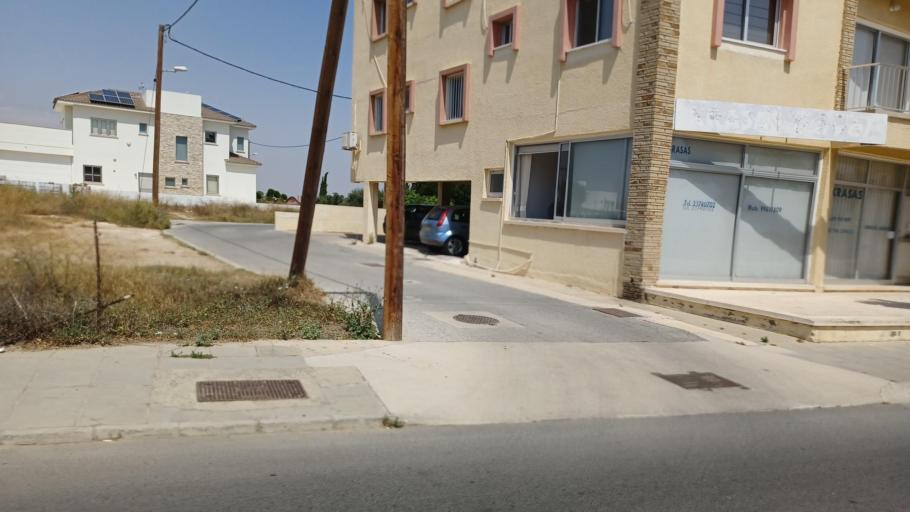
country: CY
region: Ammochostos
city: Paralimni
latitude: 35.0481
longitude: 33.9831
